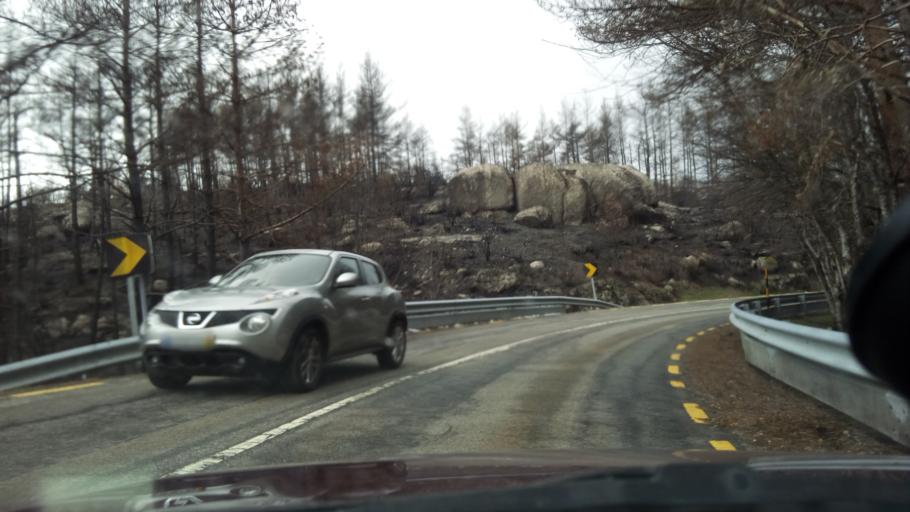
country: PT
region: Guarda
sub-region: Manteigas
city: Manteigas
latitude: 40.4116
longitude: -7.5807
